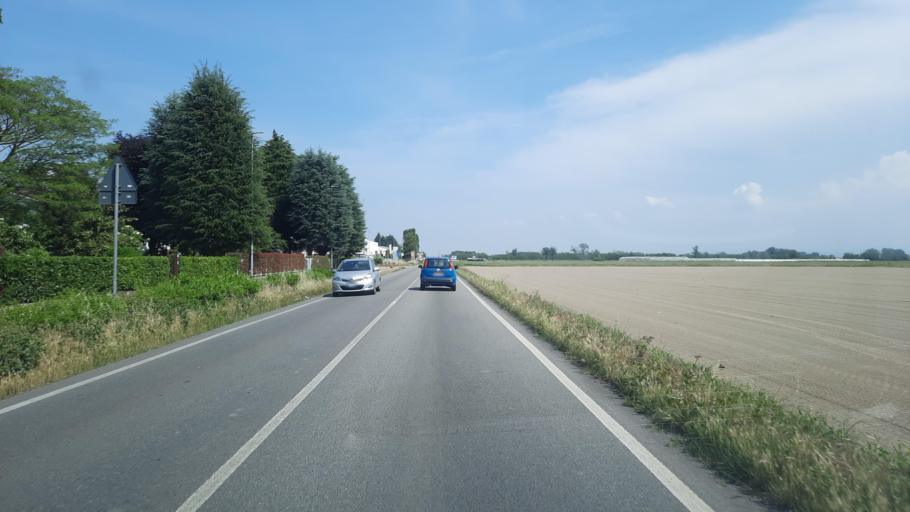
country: IT
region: Lombardy
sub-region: Provincia di Pavia
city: Carbonara al Ticino
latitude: 45.1611
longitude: 9.0714
